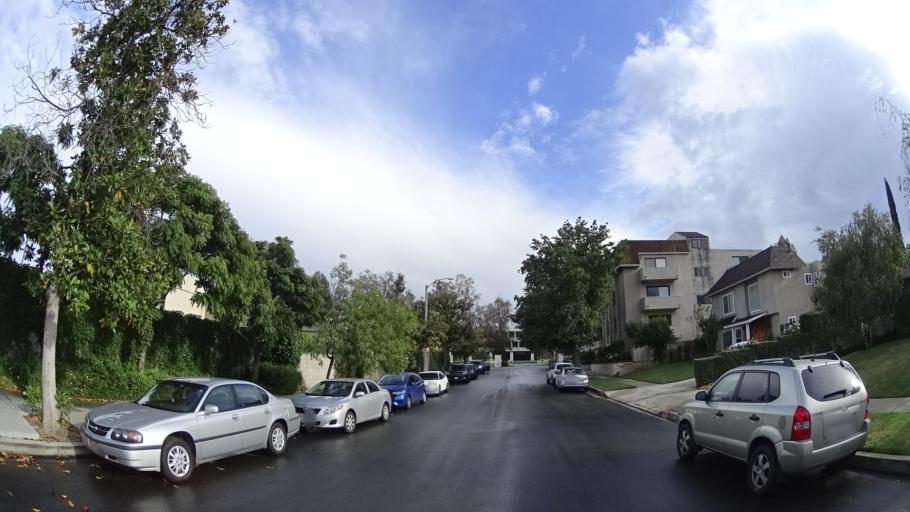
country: US
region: California
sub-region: Los Angeles County
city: Sherman Oaks
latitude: 34.1585
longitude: -118.4411
